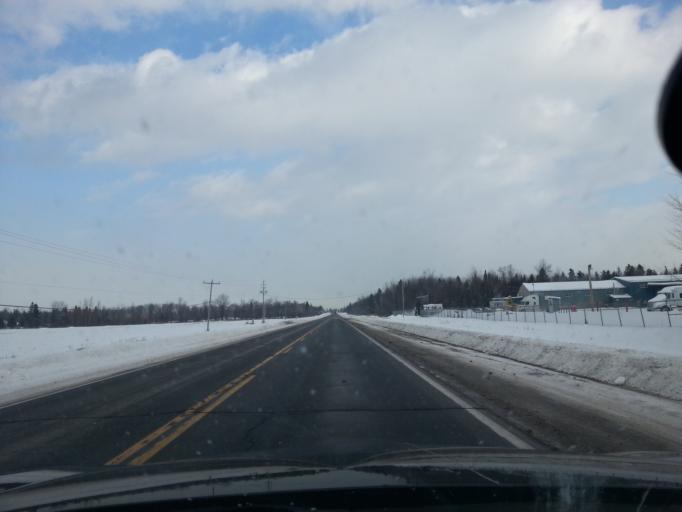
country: CA
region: Ontario
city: Bells Corners
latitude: 45.2543
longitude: -75.9576
